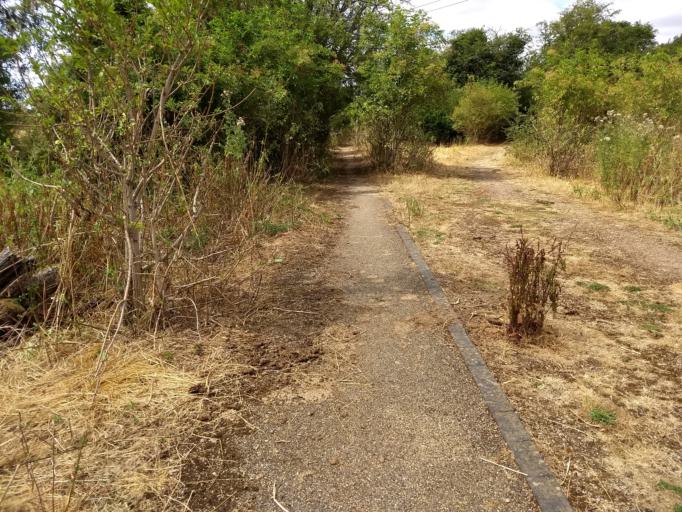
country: GB
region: England
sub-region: Milton Keynes
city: Stony Stratford
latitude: 52.0676
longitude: -0.8330
